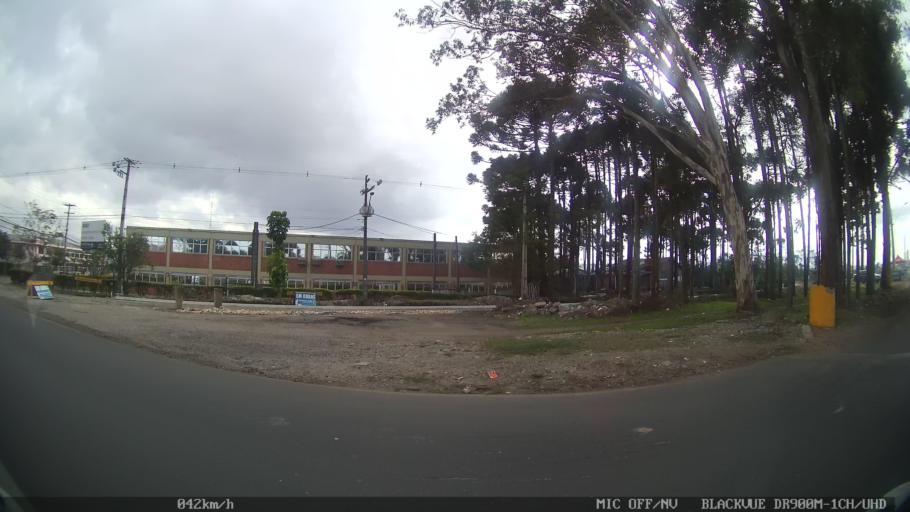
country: BR
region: Parana
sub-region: Pinhais
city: Pinhais
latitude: -25.4127
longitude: -49.1900
